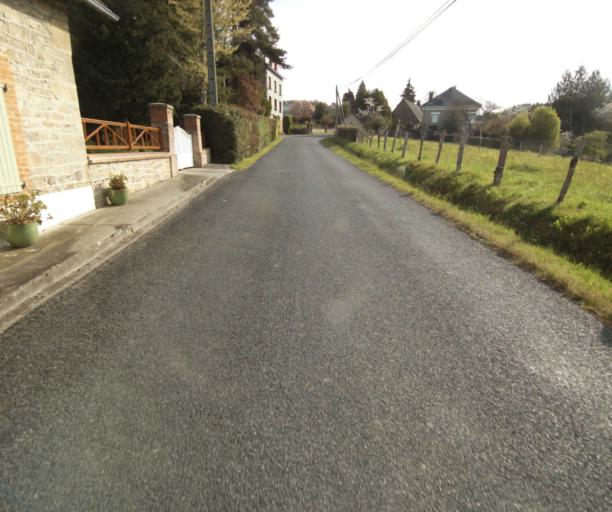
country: FR
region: Limousin
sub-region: Departement de la Correze
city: Correze
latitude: 45.3563
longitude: 1.8410
